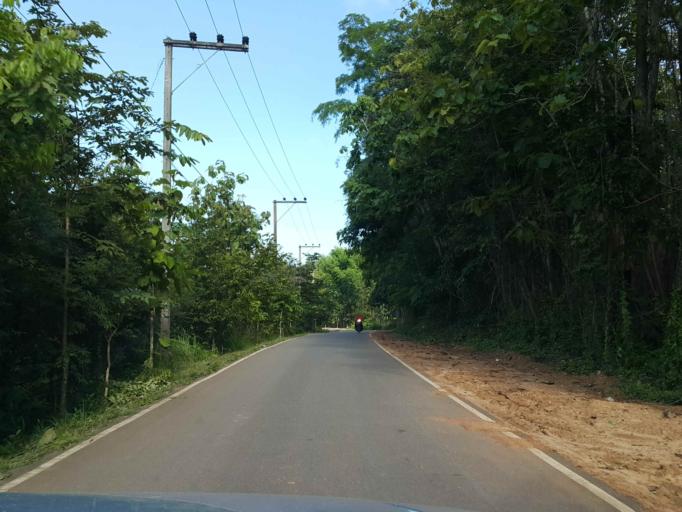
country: TH
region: Chiang Mai
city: Mae Taeng
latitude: 18.9674
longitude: 98.9060
